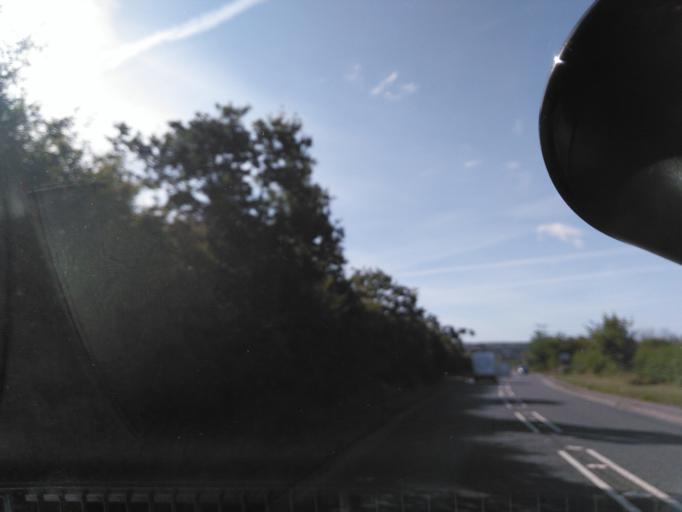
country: GB
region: England
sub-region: Wiltshire
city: Westbury
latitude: 51.2766
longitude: -2.1798
